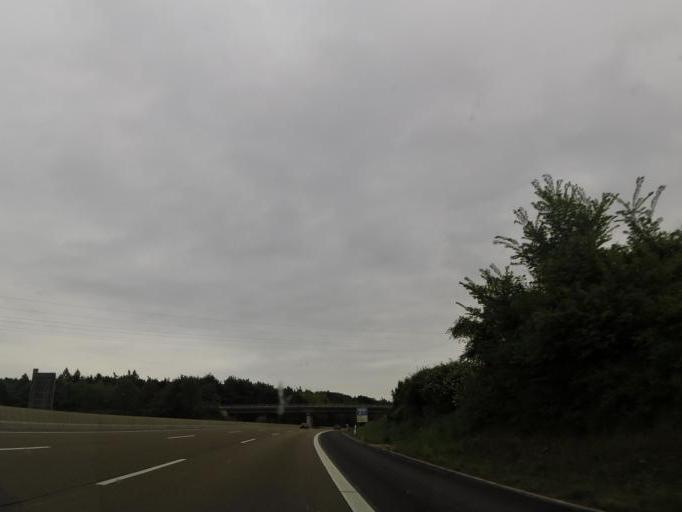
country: DE
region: Hesse
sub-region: Regierungsbezirk Kassel
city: Malsfeld
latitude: 51.0244
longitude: 9.4880
